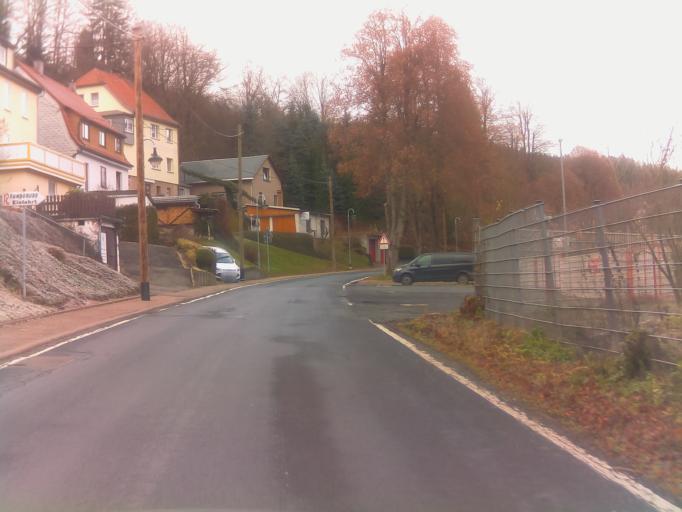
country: DE
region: Thuringia
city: Pappenheim
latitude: 50.7983
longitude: 10.4717
